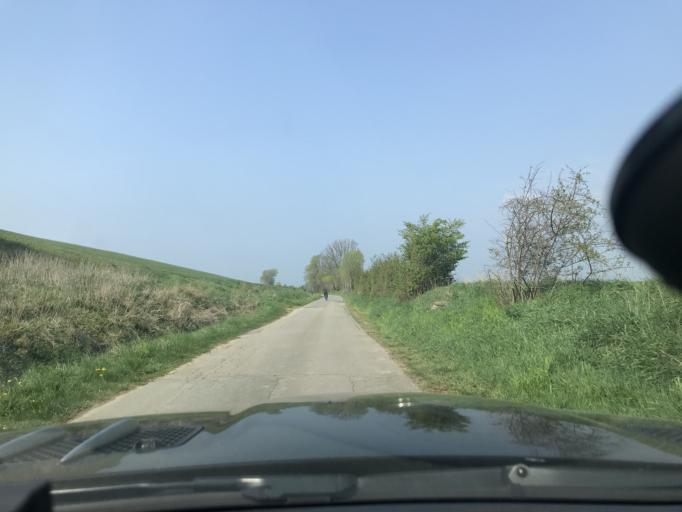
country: DE
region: Schleswig-Holstein
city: Gremersdorf
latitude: 54.3624
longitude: 10.9229
